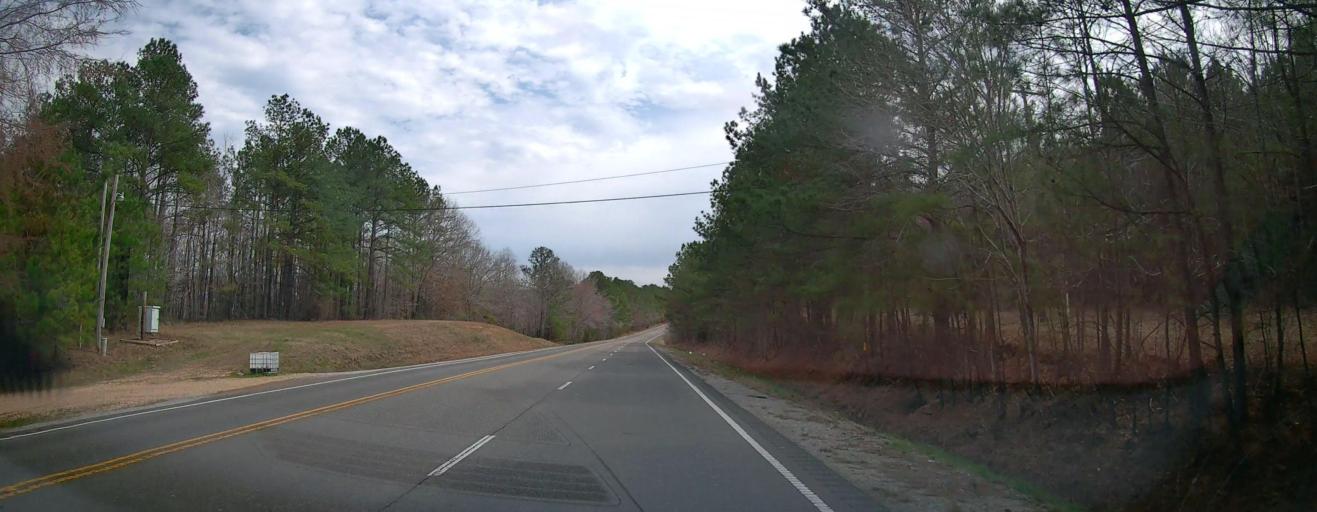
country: US
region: Alabama
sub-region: Marion County
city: Hamilton
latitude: 34.0627
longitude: -87.9697
